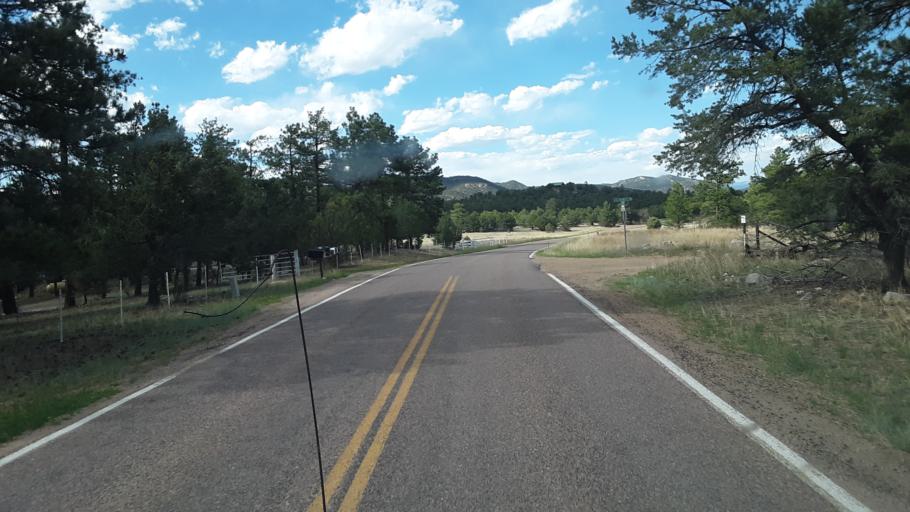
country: US
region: Colorado
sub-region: Custer County
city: Westcliffe
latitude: 38.3417
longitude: -105.4850
